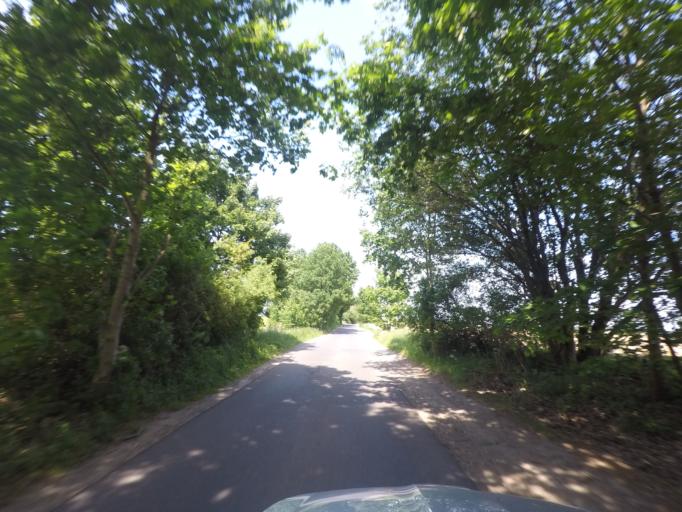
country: DE
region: Brandenburg
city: Britz
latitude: 52.8918
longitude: 13.7735
